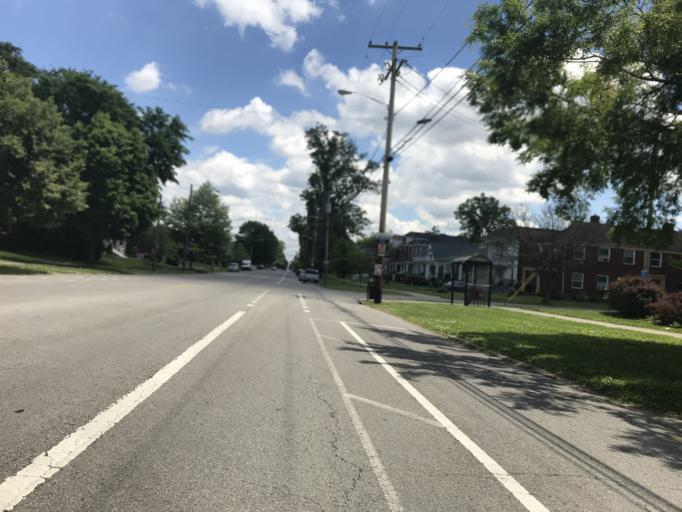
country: US
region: Indiana
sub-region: Floyd County
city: New Albany
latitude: 38.2505
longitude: -85.8256
